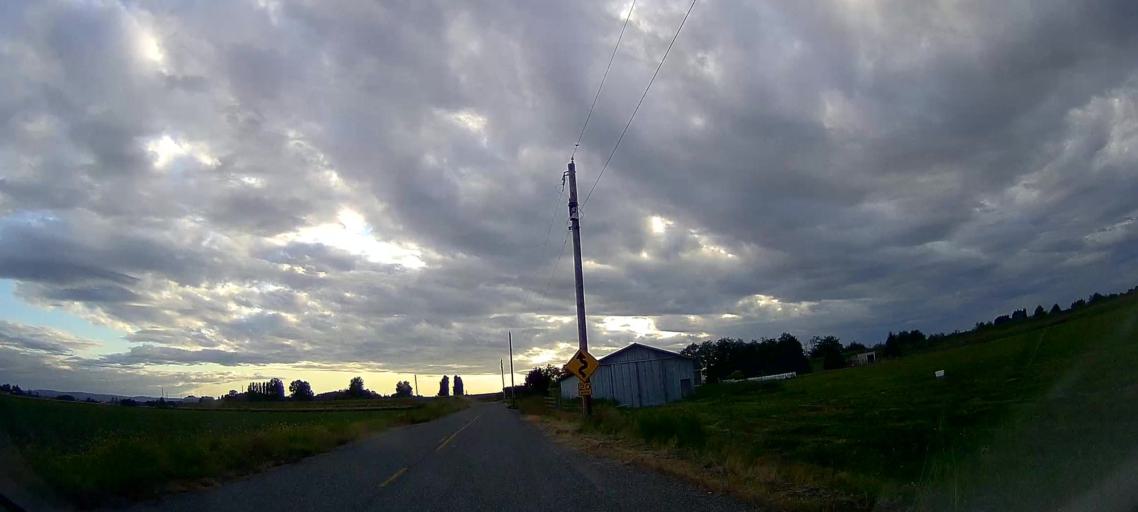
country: US
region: Washington
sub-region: Skagit County
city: Mount Vernon
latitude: 48.3701
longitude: -122.3912
